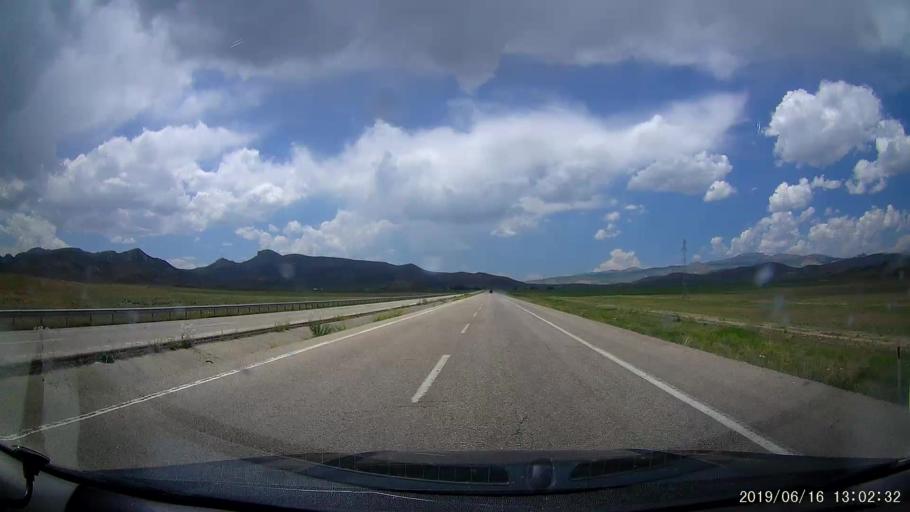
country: TR
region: Agri
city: Sulucem
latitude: 39.5752
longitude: 43.8137
